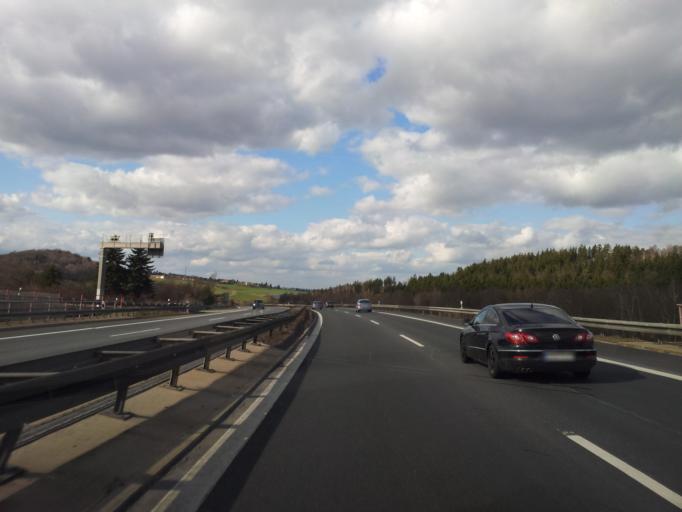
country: DE
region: Saxony
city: Theuma
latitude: 50.4678
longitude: 12.1864
